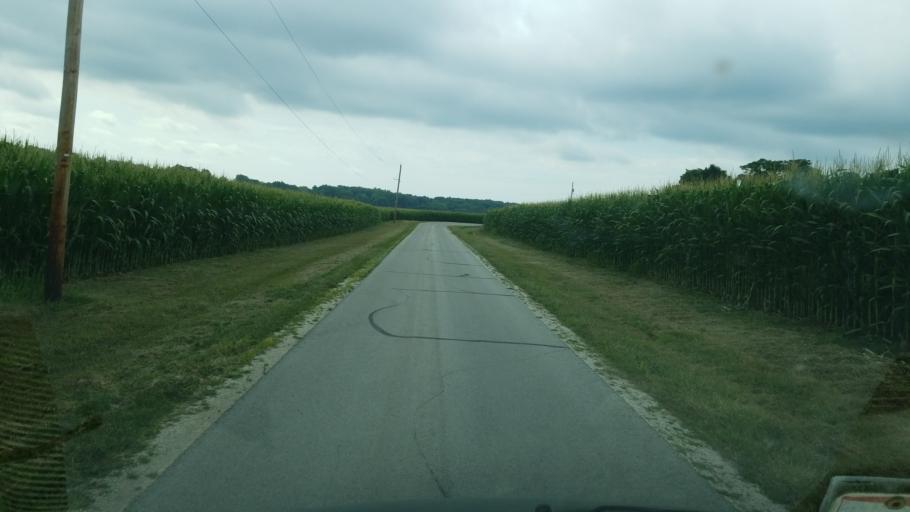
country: US
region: Ohio
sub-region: Sandusky County
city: Green Springs
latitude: 41.2173
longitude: -83.1355
